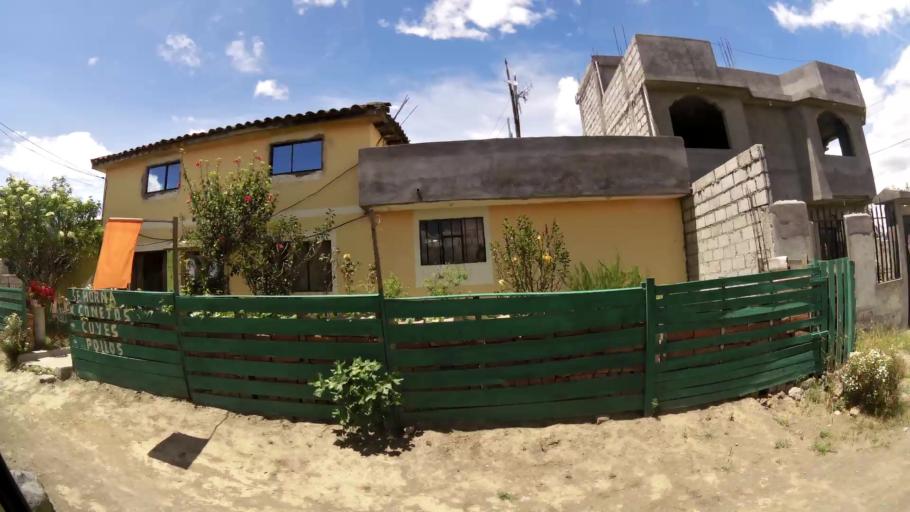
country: EC
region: Tungurahua
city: Ambato
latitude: -1.2802
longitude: -78.5988
